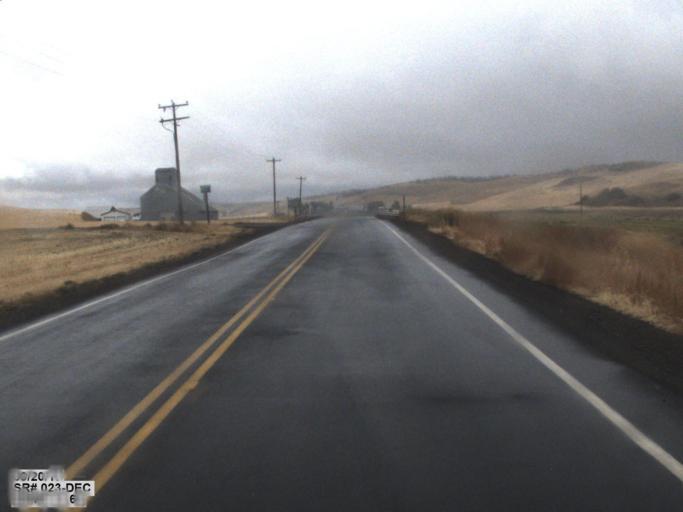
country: US
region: Washington
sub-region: Whitman County
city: Colfax
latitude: 47.0757
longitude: -117.5369
